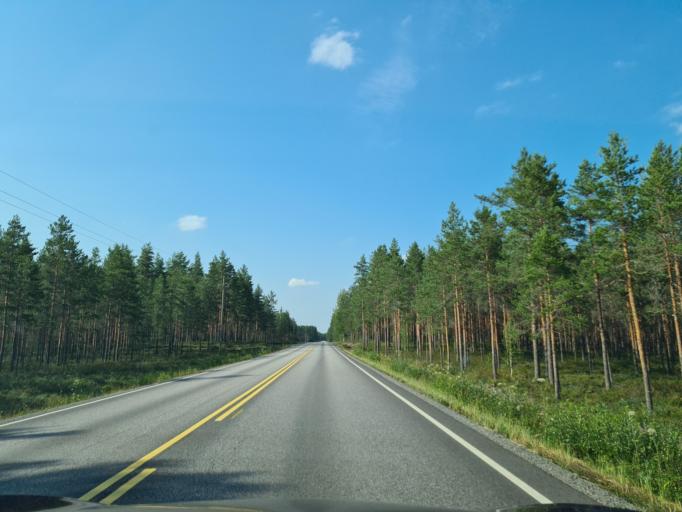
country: FI
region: Satakunta
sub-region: Pohjois-Satakunta
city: Karvia
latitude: 62.0631
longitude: 22.5113
